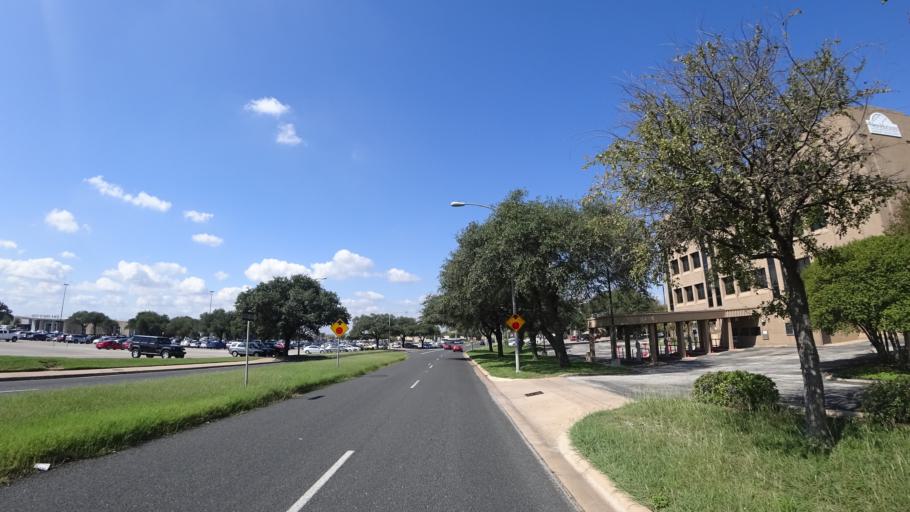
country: US
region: Texas
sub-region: Travis County
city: Austin
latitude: 30.3286
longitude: -97.7118
